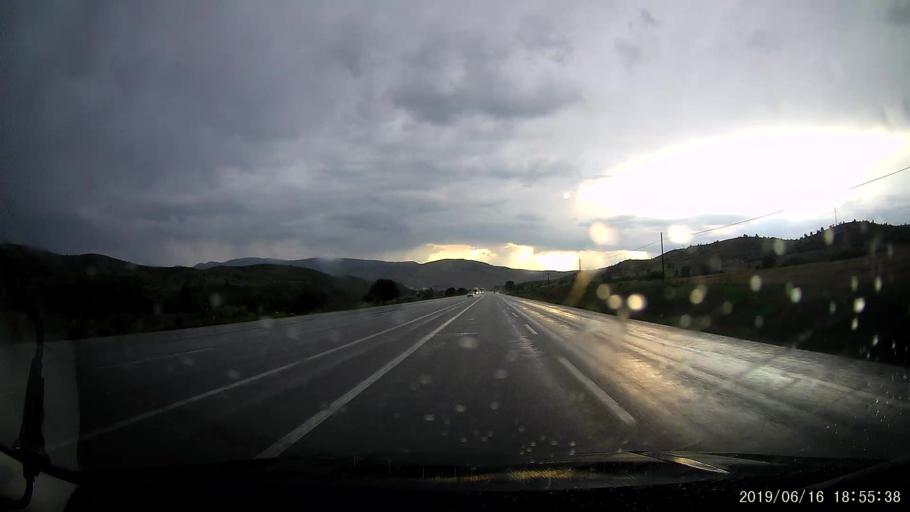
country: TR
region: Erzincan
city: Refahiye
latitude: 39.9011
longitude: 38.8225
